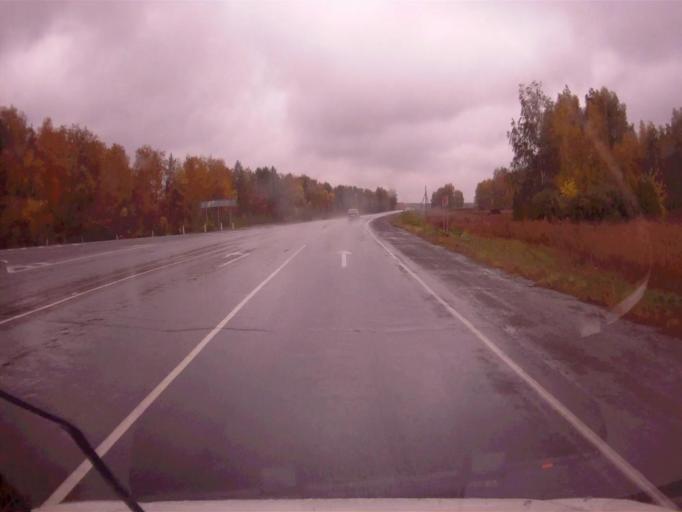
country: RU
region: Chelyabinsk
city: Roshchino
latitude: 55.4000
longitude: 61.0750
